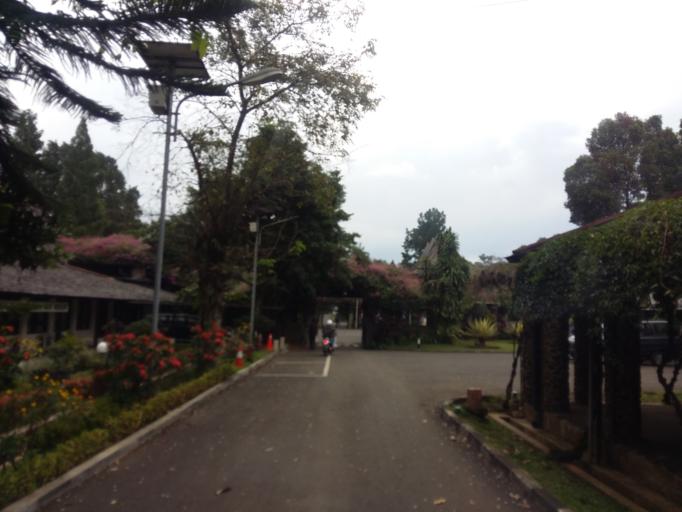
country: ID
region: West Java
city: Bandung
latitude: -6.8927
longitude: 107.6111
